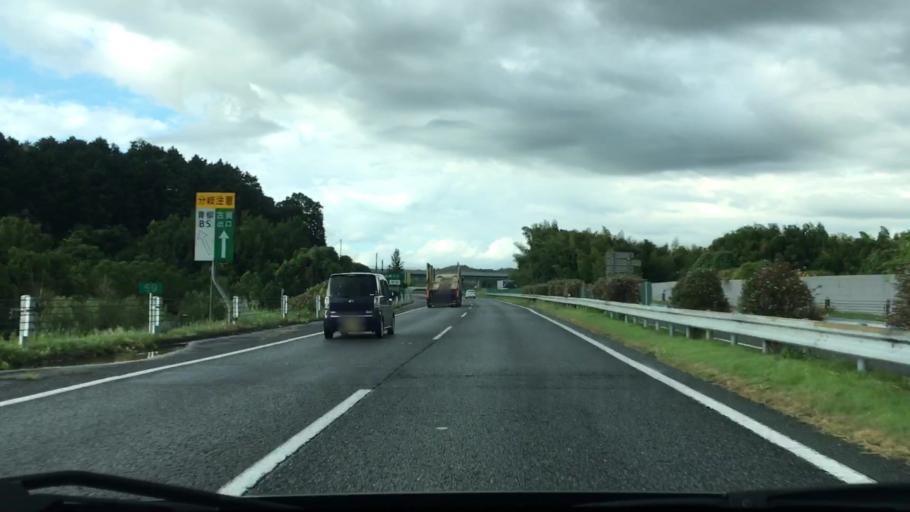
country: JP
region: Fukuoka
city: Koga
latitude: 33.7091
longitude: 130.4877
